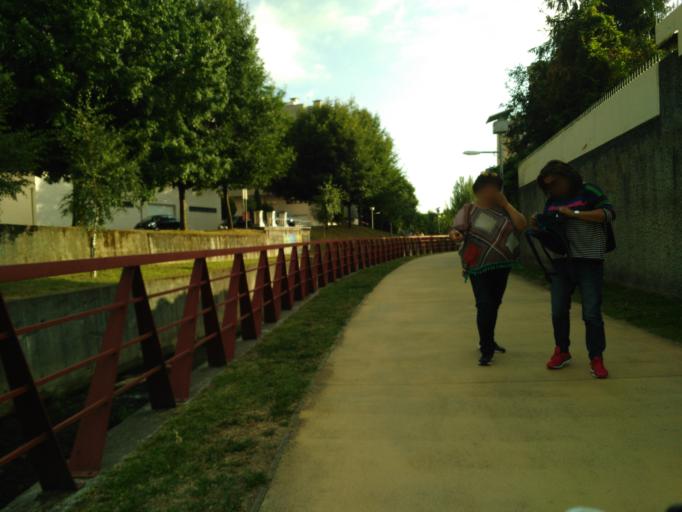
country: PT
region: Braga
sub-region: Braga
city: Braga
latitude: 41.5486
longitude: -8.4080
